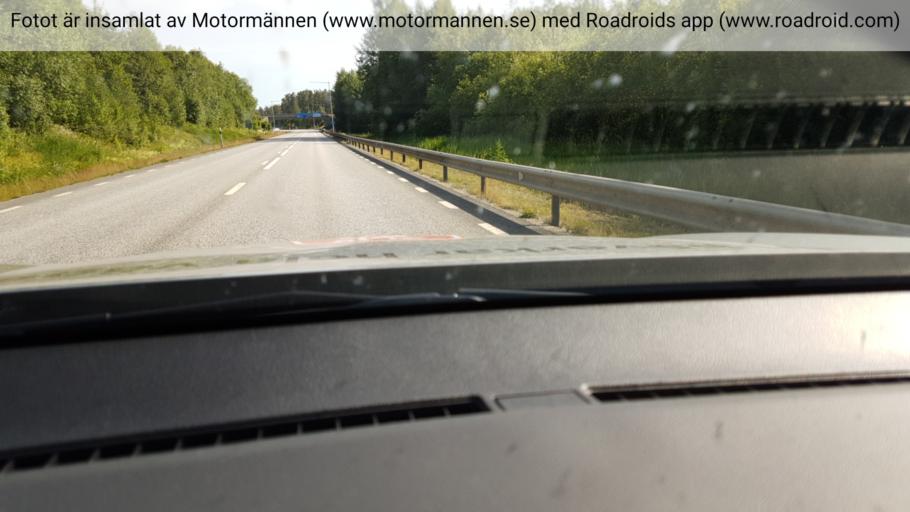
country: SE
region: Joenkoeping
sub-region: Eksjo Kommun
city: Eksjoe
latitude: 57.6804
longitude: 14.9534
